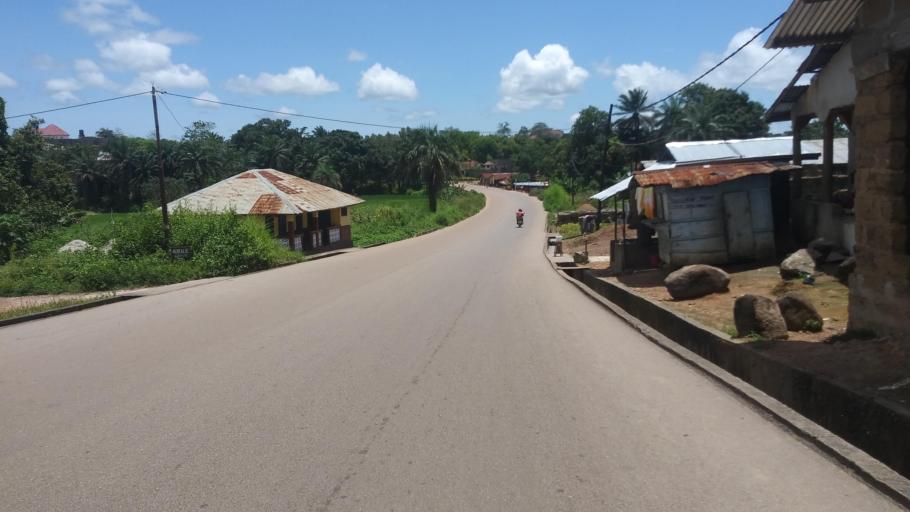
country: SL
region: Northern Province
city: Makeni
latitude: 8.8794
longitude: -12.0298
